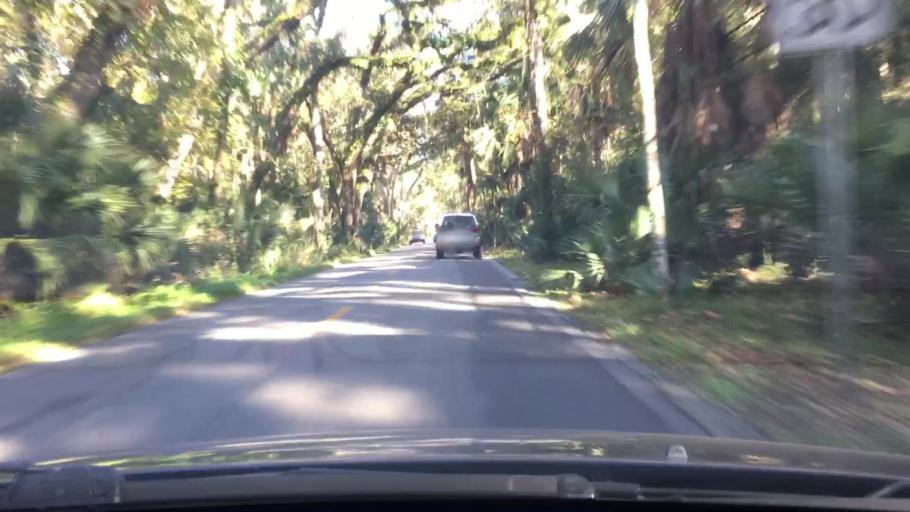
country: US
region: Florida
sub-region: Flagler County
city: Flagler Beach
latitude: 29.4046
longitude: -81.1326
